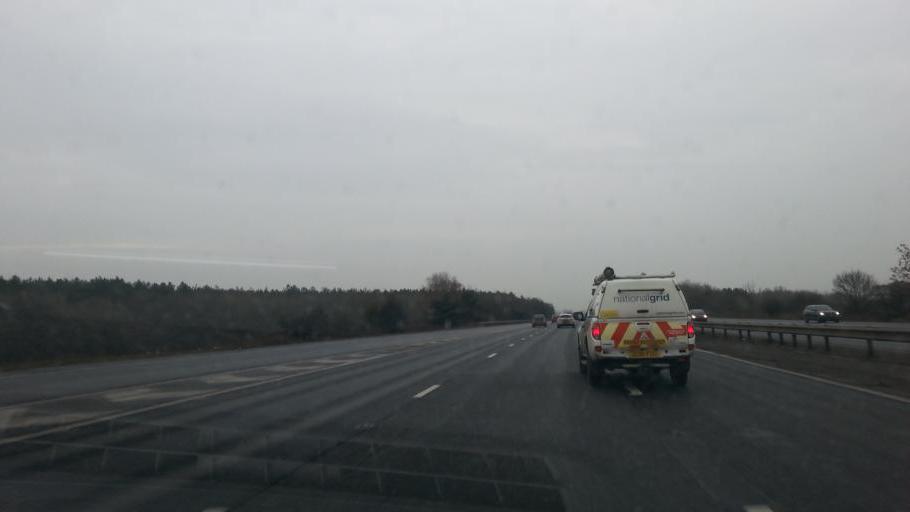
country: GB
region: England
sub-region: Essex
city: Harlow
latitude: 51.7458
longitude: 0.1393
